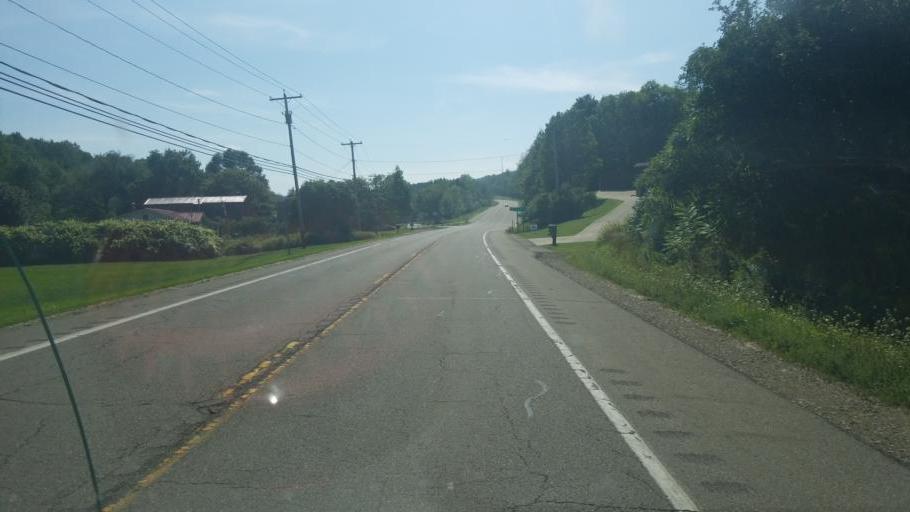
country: US
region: New York
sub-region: Allegany County
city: Wellsville
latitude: 42.1206
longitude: -78.0009
